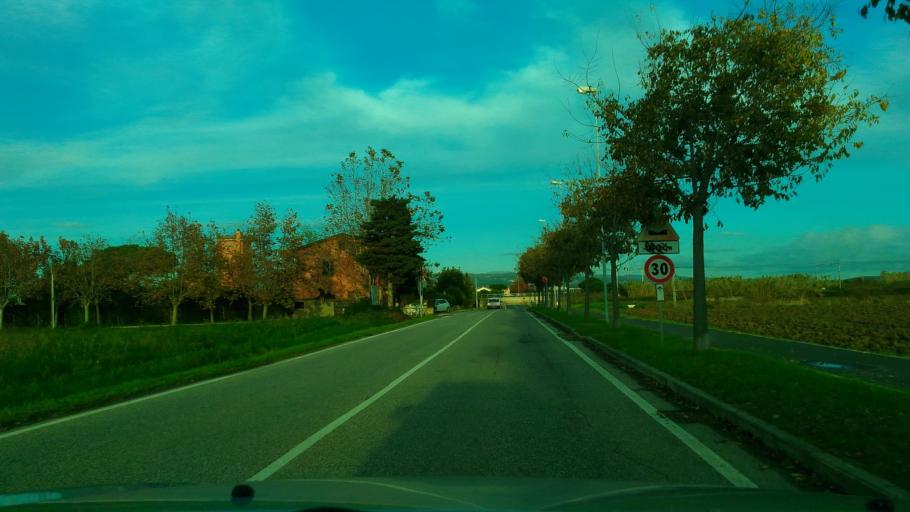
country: IT
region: Tuscany
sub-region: Provincia di Livorno
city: S.P. in Palazzi
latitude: 43.3203
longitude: 10.5024
